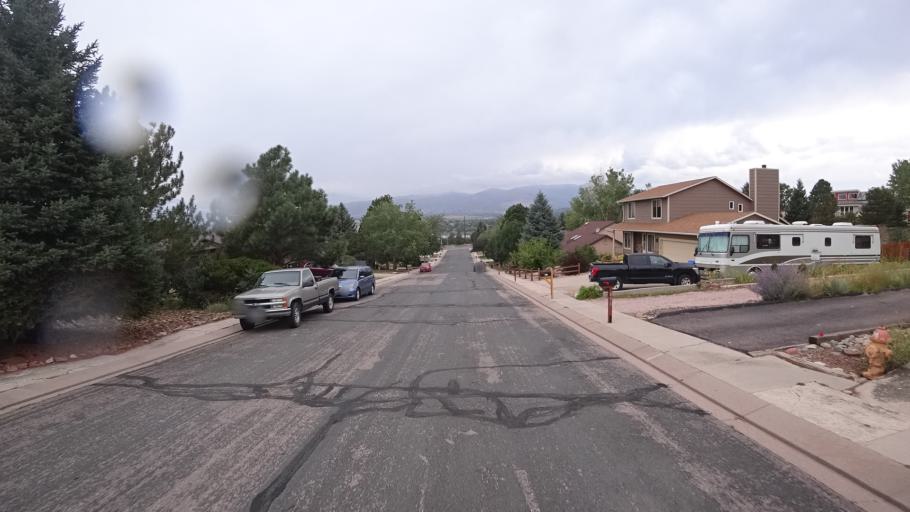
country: US
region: Colorado
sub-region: El Paso County
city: Colorado Springs
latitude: 38.9193
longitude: -104.8104
